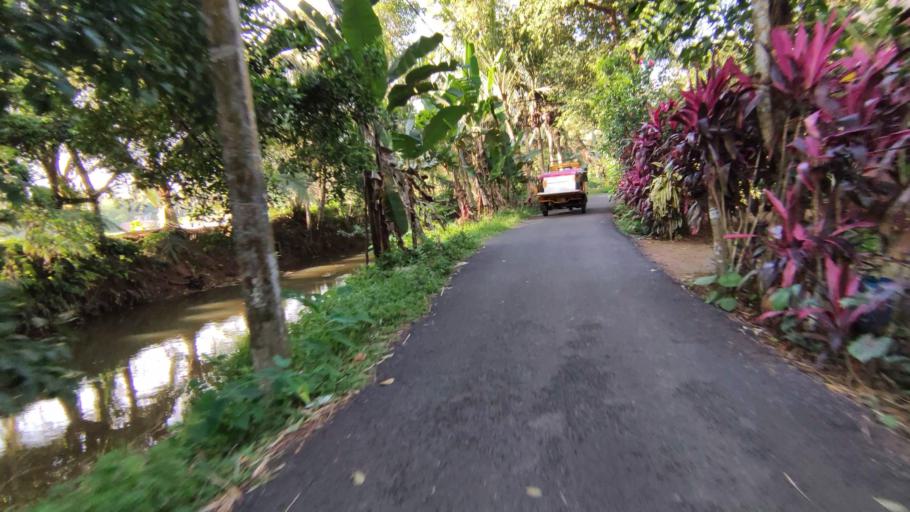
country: IN
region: Kerala
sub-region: Kottayam
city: Kottayam
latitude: 9.5953
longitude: 76.4865
